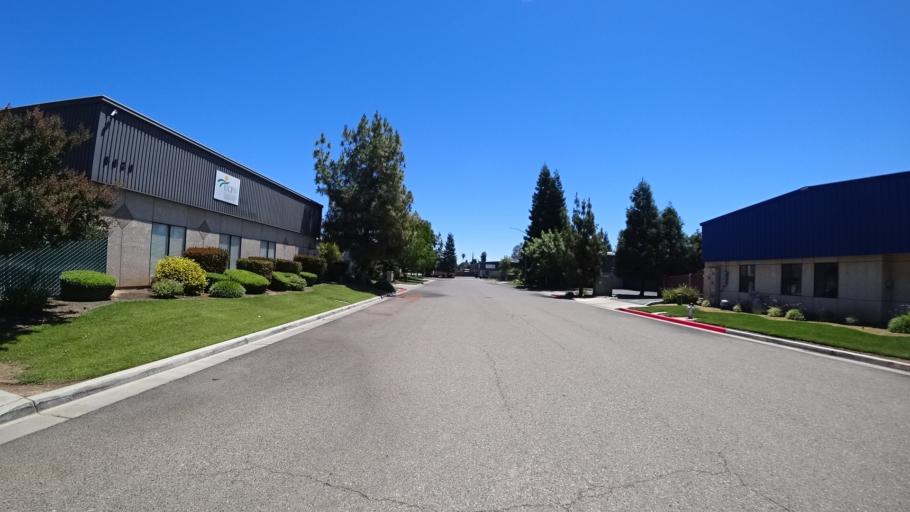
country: US
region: California
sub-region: Fresno County
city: West Park
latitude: 36.8009
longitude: -119.8577
